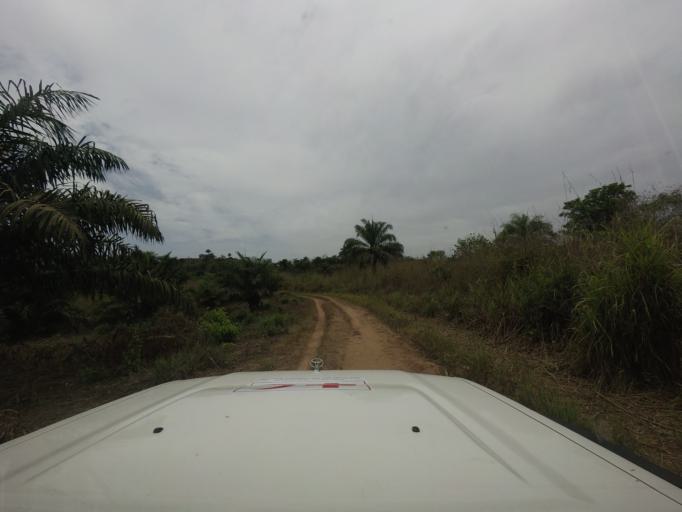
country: SL
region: Eastern Province
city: Buedu
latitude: 8.2615
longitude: -10.2880
